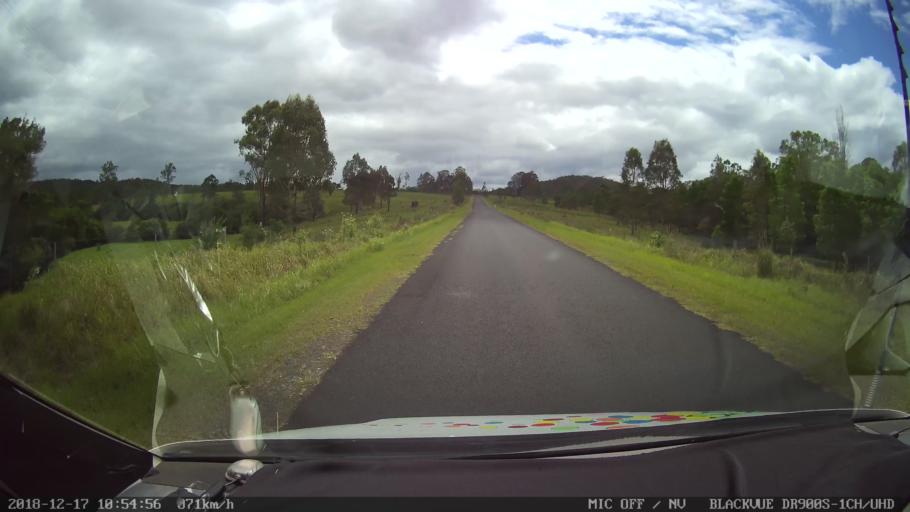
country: AU
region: New South Wales
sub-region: Tenterfield Municipality
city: Carrolls Creek
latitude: -28.8280
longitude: 152.5731
